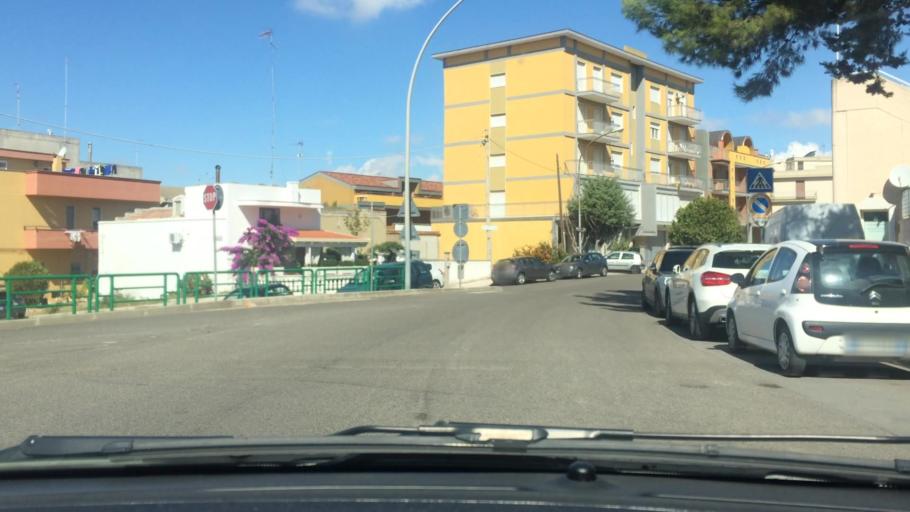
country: IT
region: Basilicate
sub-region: Provincia di Matera
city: Montescaglioso
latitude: 40.5456
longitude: 16.6671
